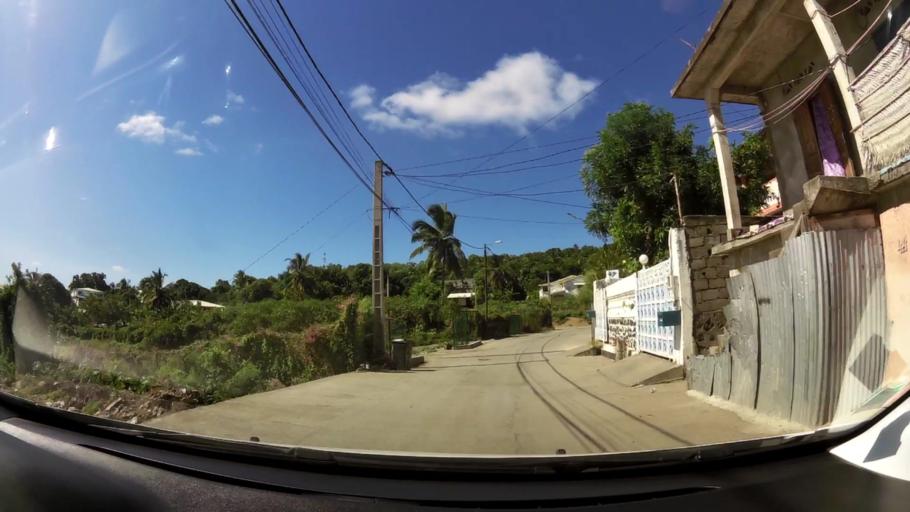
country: YT
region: Pamandzi
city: Pamandzi
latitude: -12.7867
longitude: 45.2806
